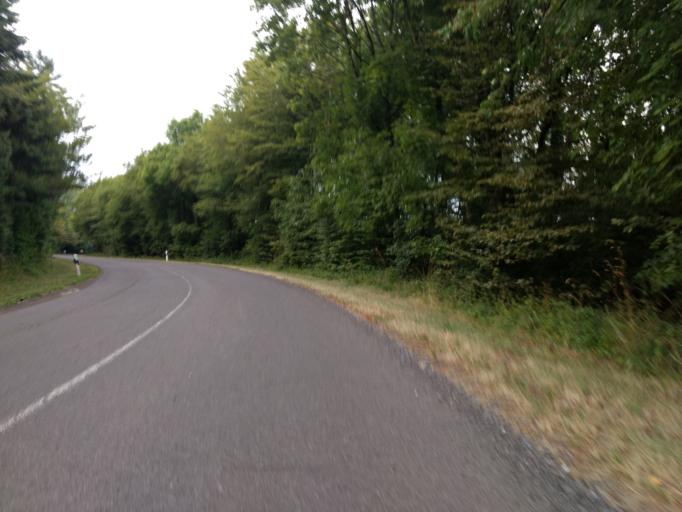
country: DE
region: Saarland
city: Rehlingen-Siersburg
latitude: 49.3209
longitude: 6.6661
